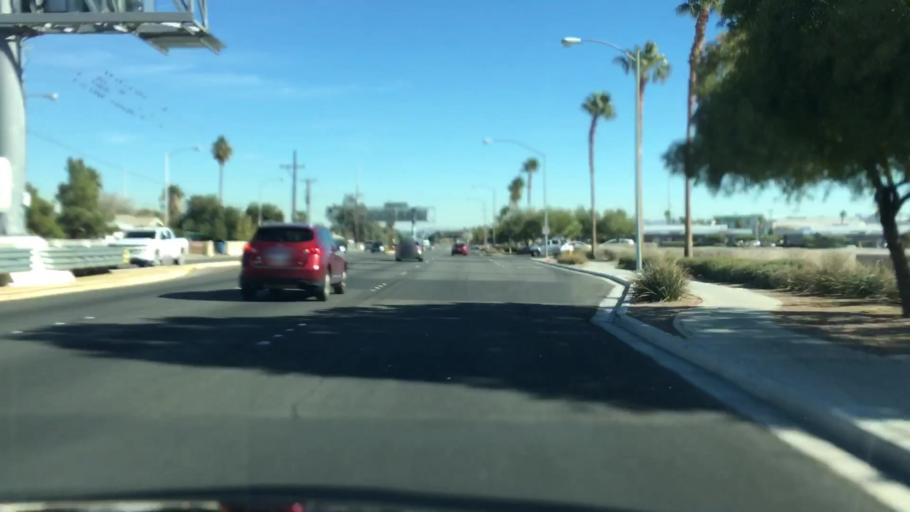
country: US
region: Nevada
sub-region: Clark County
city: Paradise
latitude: 36.0862
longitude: -115.1224
